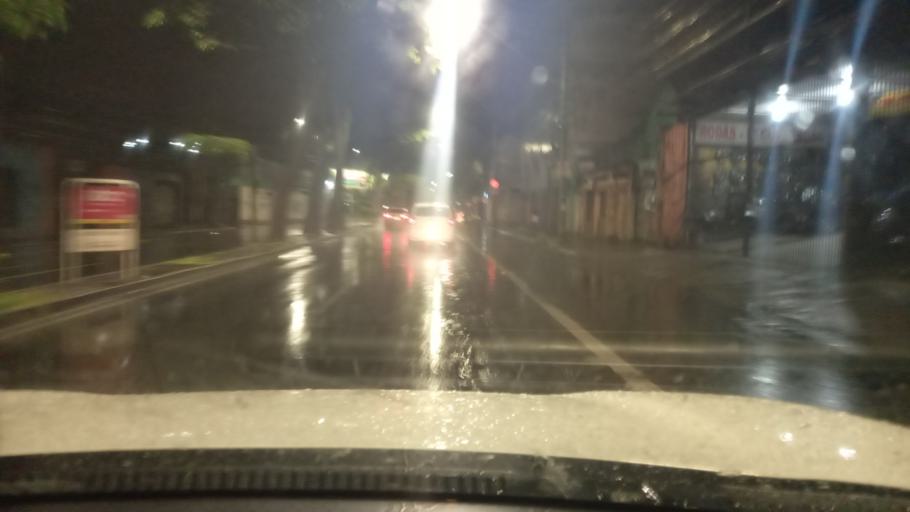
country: BR
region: Minas Gerais
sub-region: Belo Horizonte
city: Belo Horizonte
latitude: -19.9089
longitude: -43.9579
